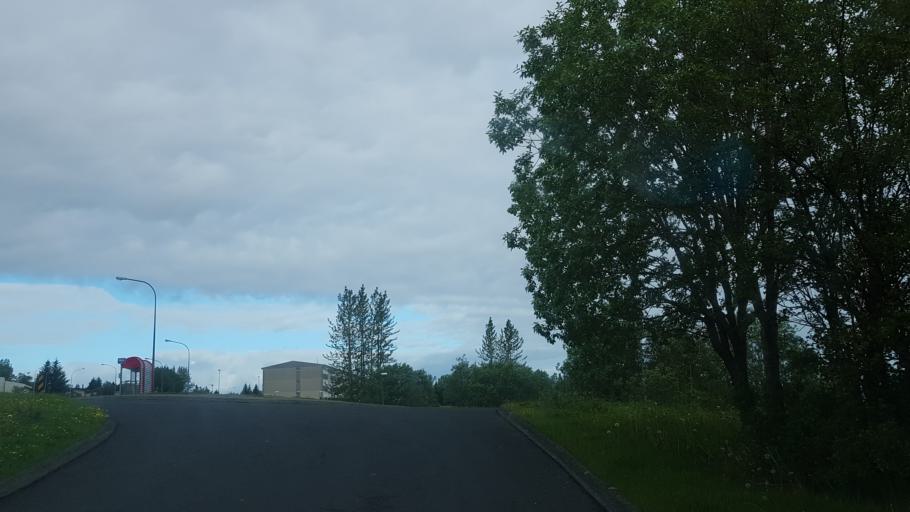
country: IS
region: Capital Region
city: Reykjavik
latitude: 64.0982
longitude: -21.8457
